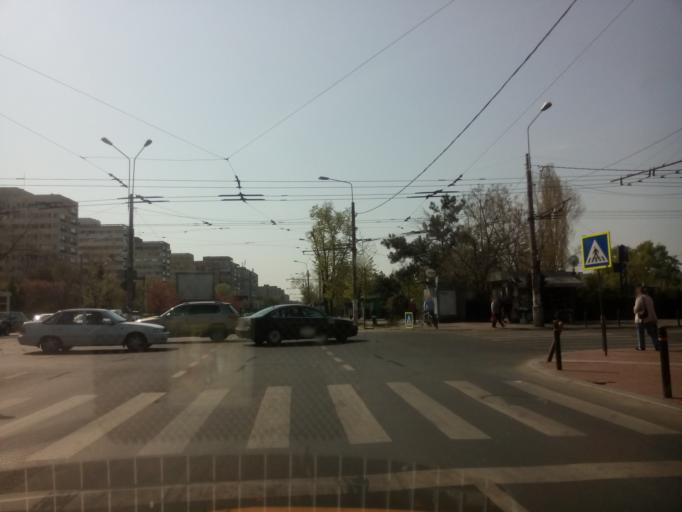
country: RO
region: Ilfov
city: Dobroesti
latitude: 44.4295
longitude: 26.1620
